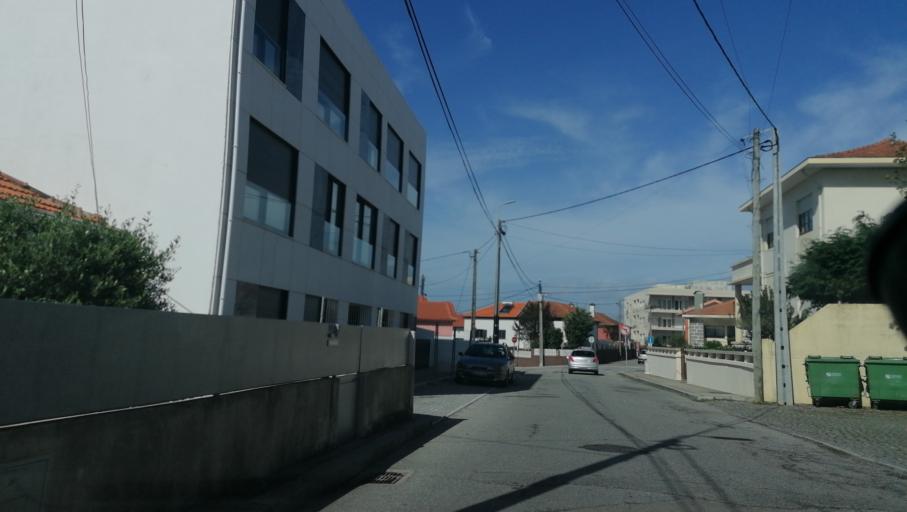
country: PT
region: Aveiro
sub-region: Espinho
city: Espinho
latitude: 41.0108
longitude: -8.6319
